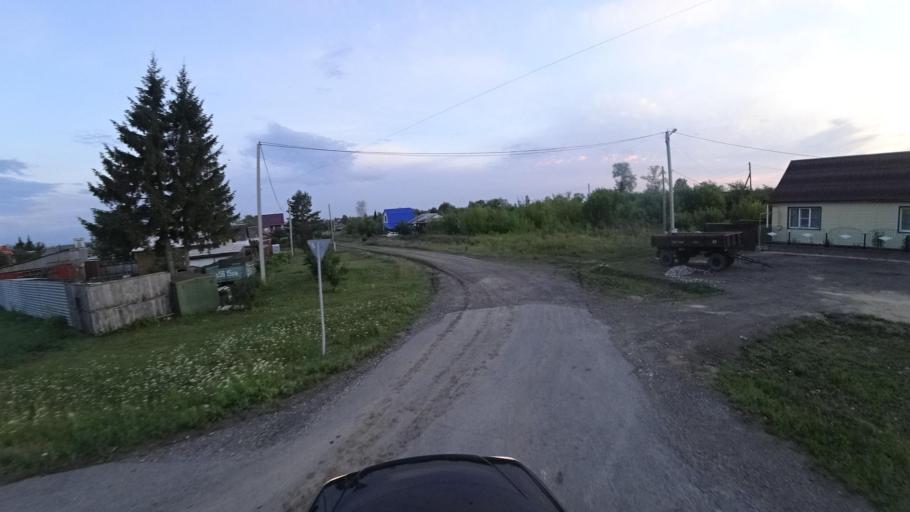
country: RU
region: Sverdlovsk
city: Kamyshlov
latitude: 56.8556
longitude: 62.7347
